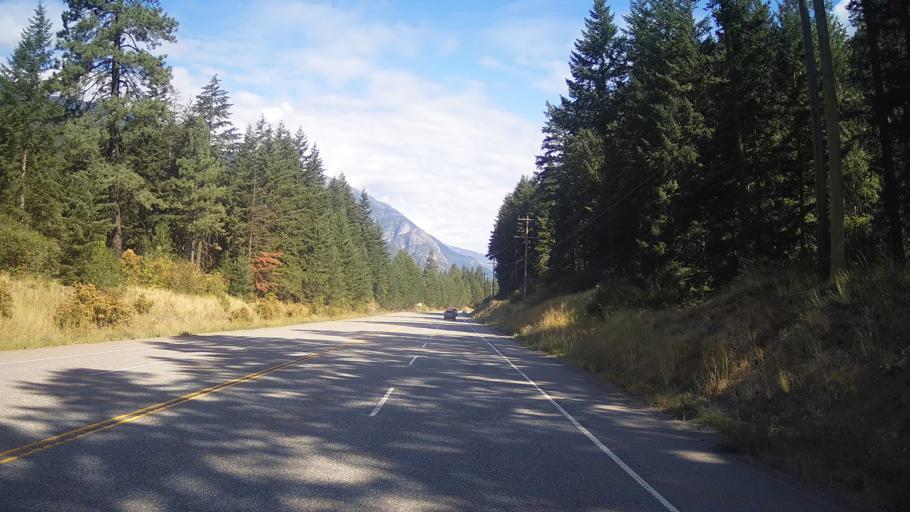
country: CA
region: British Columbia
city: Hope
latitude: 50.0470
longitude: -121.5393
